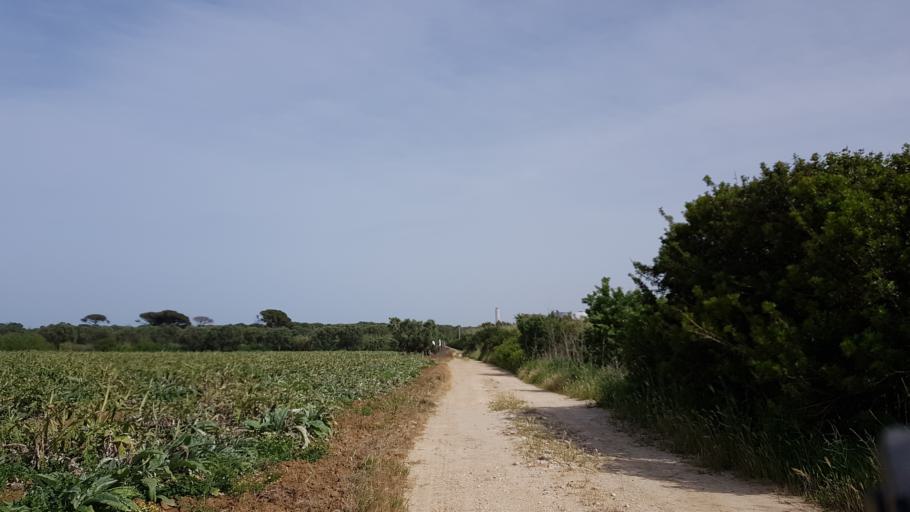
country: IT
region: Apulia
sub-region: Provincia di Brindisi
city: La Rosa
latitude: 40.5912
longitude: 17.9989
